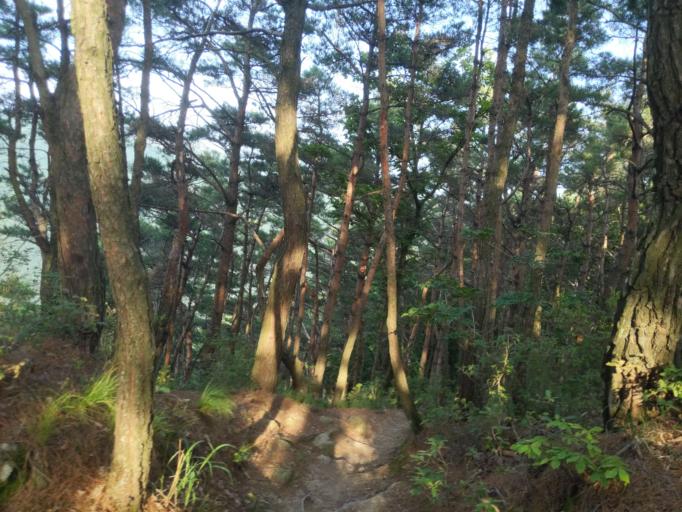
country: KR
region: Daegu
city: Hwawon
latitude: 35.7834
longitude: 128.5465
